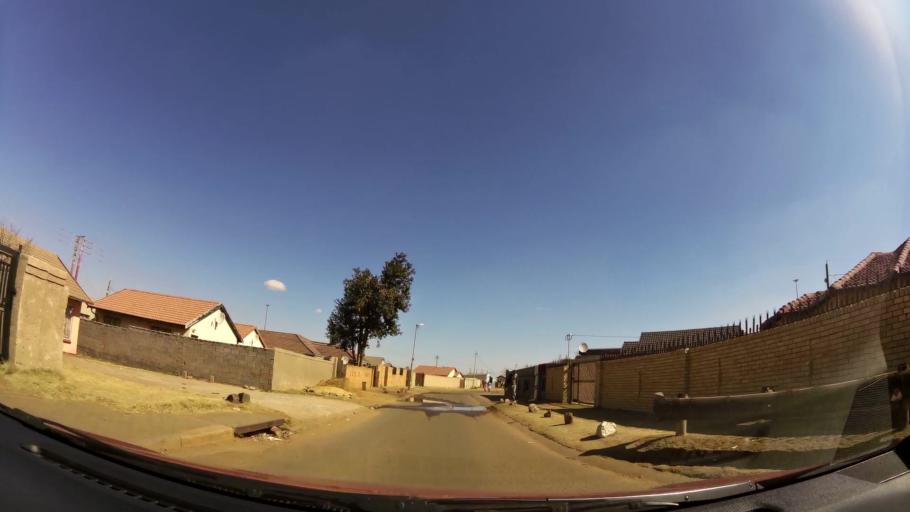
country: ZA
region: Gauteng
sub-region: City of Johannesburg Metropolitan Municipality
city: Soweto
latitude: -26.2509
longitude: 27.8077
